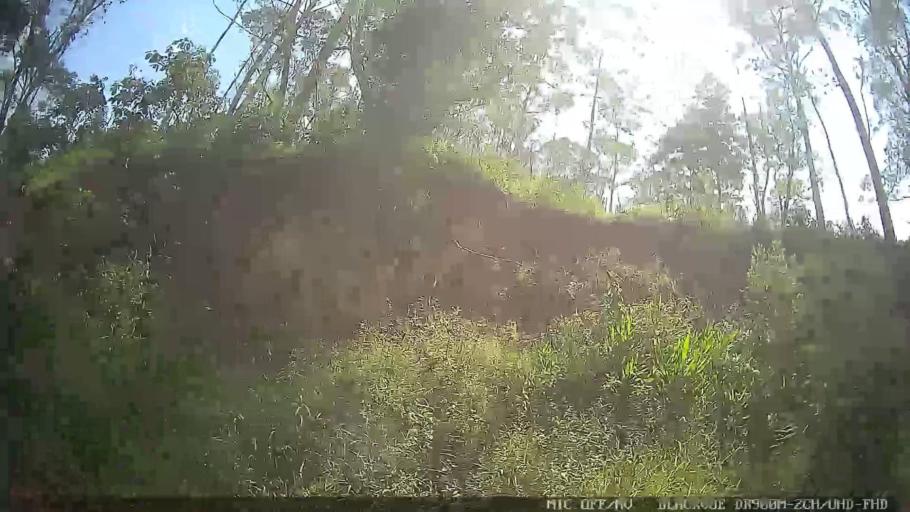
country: BR
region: Sao Paulo
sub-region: Ribeirao Pires
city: Ribeirao Pires
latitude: -23.6491
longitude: -46.3684
